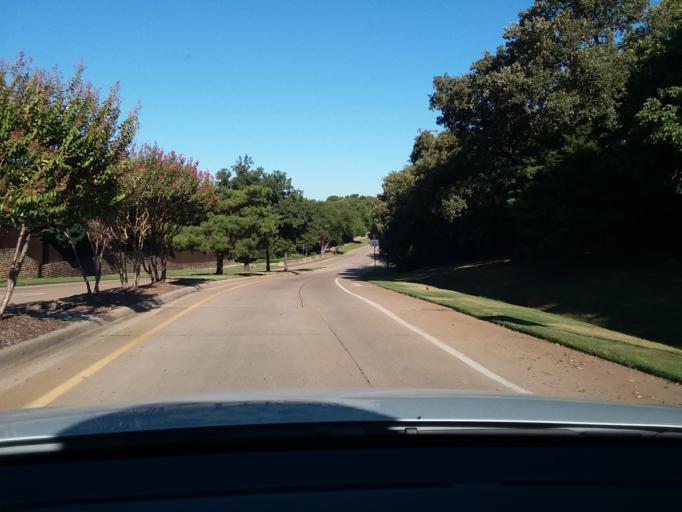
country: US
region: Texas
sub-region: Denton County
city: Highland Village
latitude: 33.0858
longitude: -97.0664
